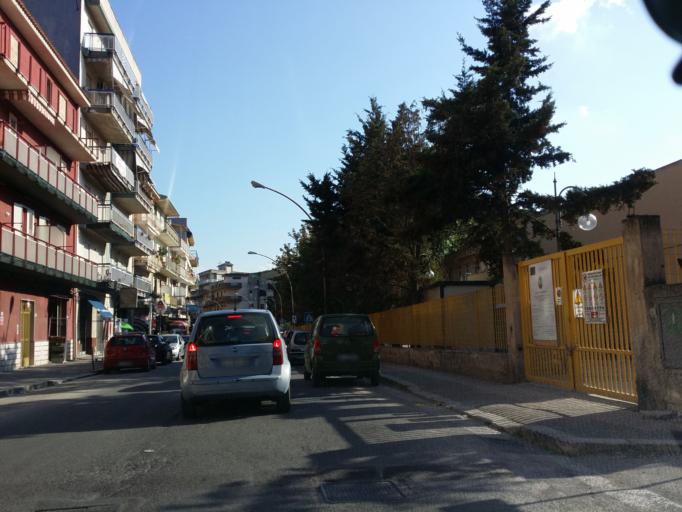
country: IT
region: Sicily
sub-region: Palermo
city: Misilmeri
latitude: 38.0320
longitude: 13.4505
